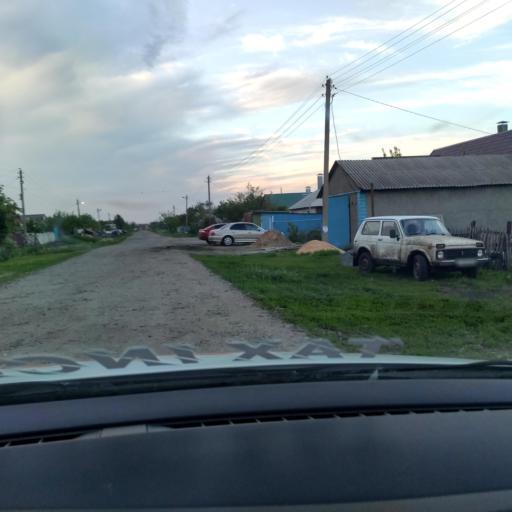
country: RU
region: Voronezj
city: Maslovka
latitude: 51.4512
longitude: 39.2370
